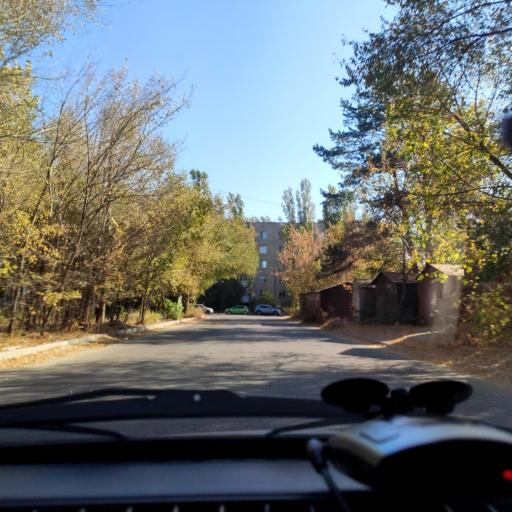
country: RU
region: Voronezj
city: Voronezh
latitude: 51.6896
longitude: 39.1433
